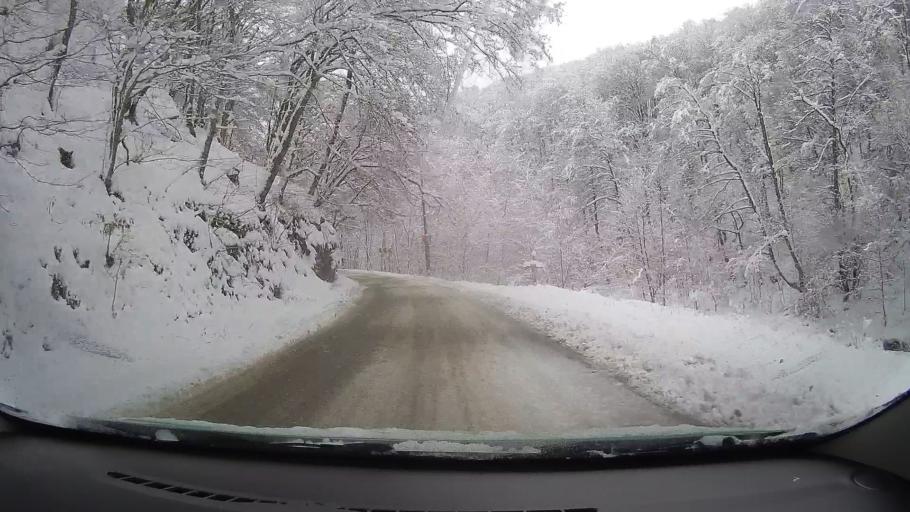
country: RO
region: Alba
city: Pianu de Sus
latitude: 45.8714
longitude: 23.4927
